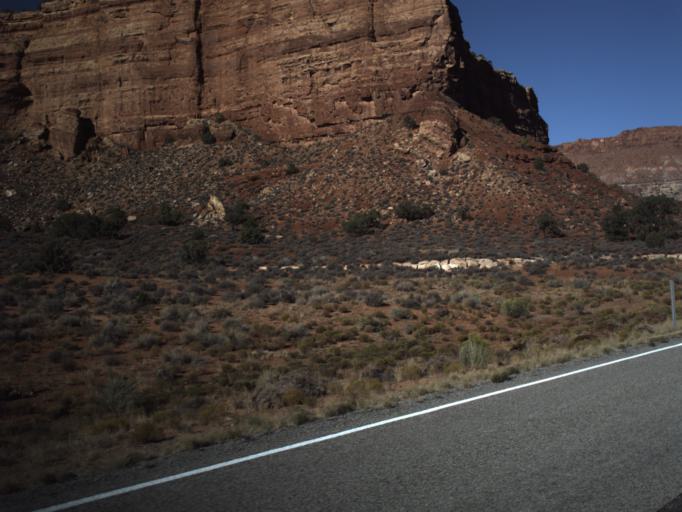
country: US
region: Utah
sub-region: San Juan County
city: Blanding
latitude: 37.7342
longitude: -110.2656
